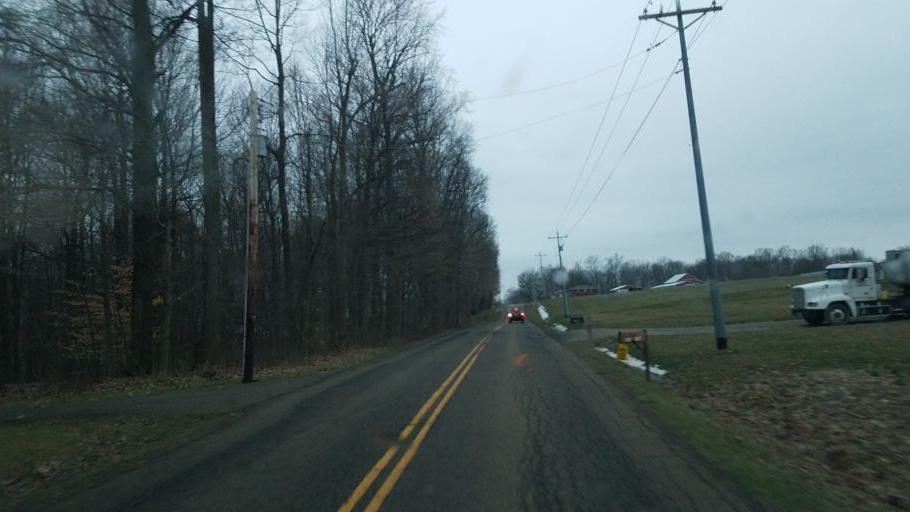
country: US
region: Ohio
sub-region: Knox County
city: Fredericktown
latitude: 40.4951
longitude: -82.4327
